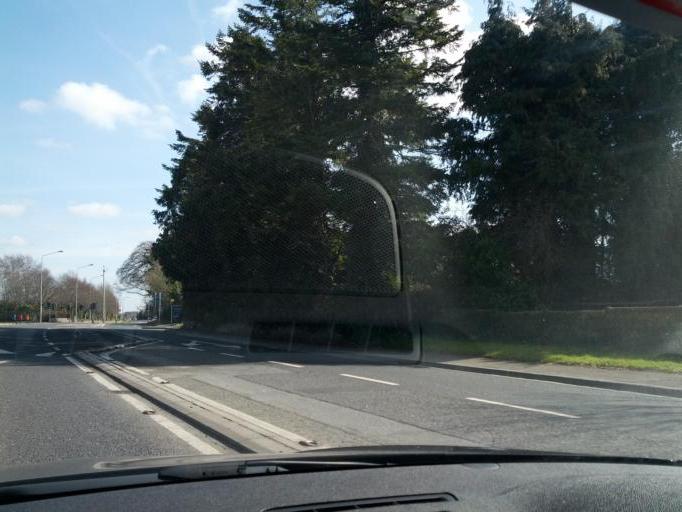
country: IE
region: Leinster
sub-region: Kildare
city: Leixlip
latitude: 53.3746
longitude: -6.5296
